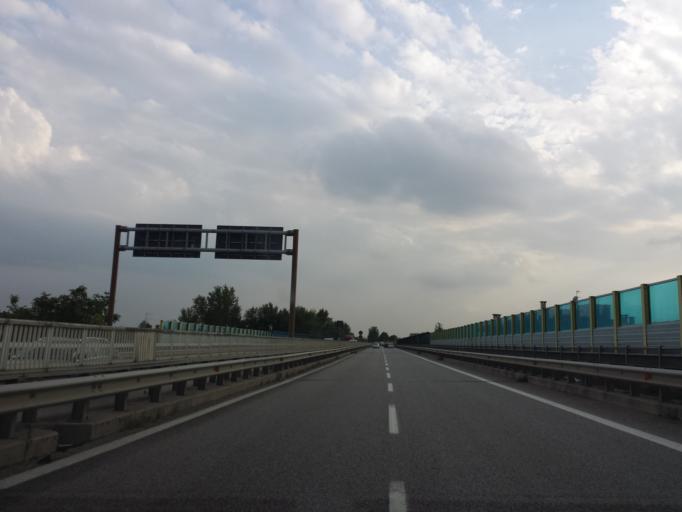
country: IT
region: Veneto
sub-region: Provincia di Padova
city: Cadoneghe
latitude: 45.4383
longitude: 11.9279
